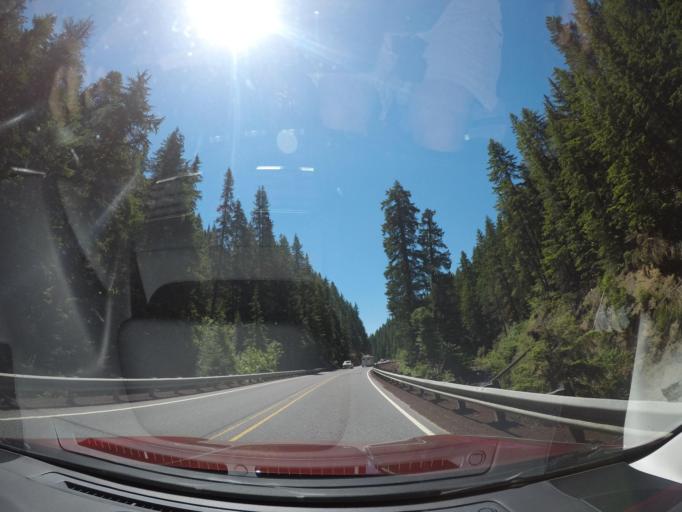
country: US
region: Oregon
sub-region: Deschutes County
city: Sisters
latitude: 44.5522
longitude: -121.9938
